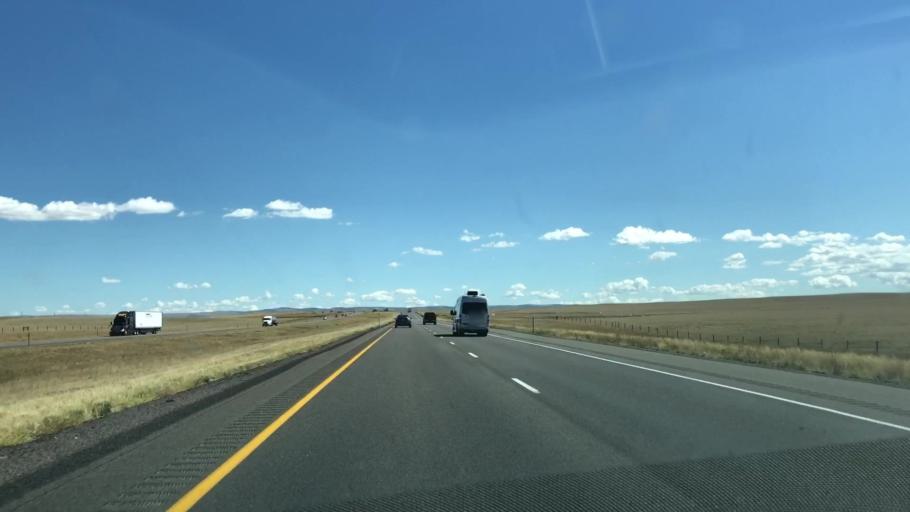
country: US
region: Wyoming
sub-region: Albany County
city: Laramie
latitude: 41.3577
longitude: -105.7554
